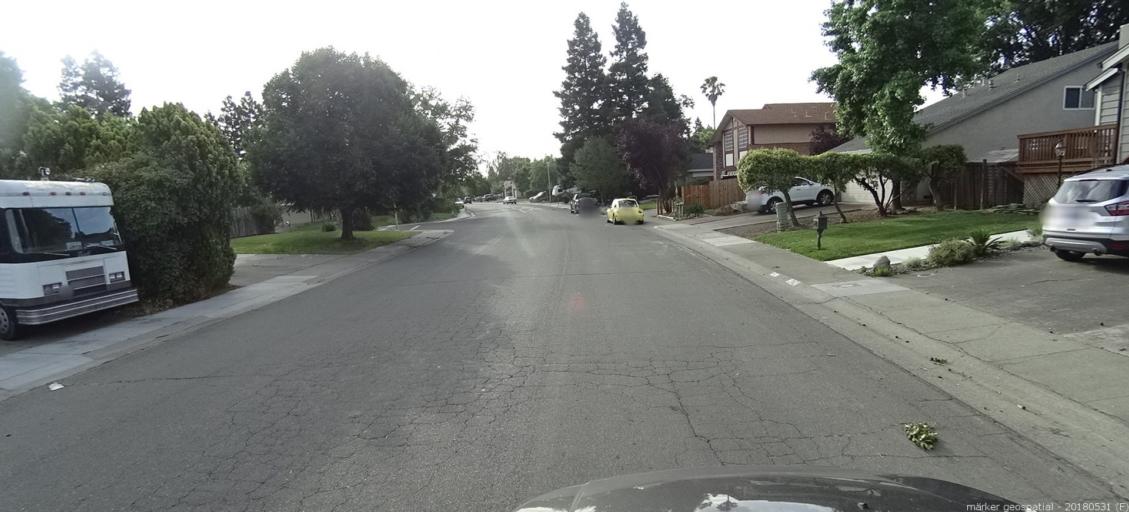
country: US
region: California
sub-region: Sacramento County
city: Sacramento
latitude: 38.6228
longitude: -121.4920
